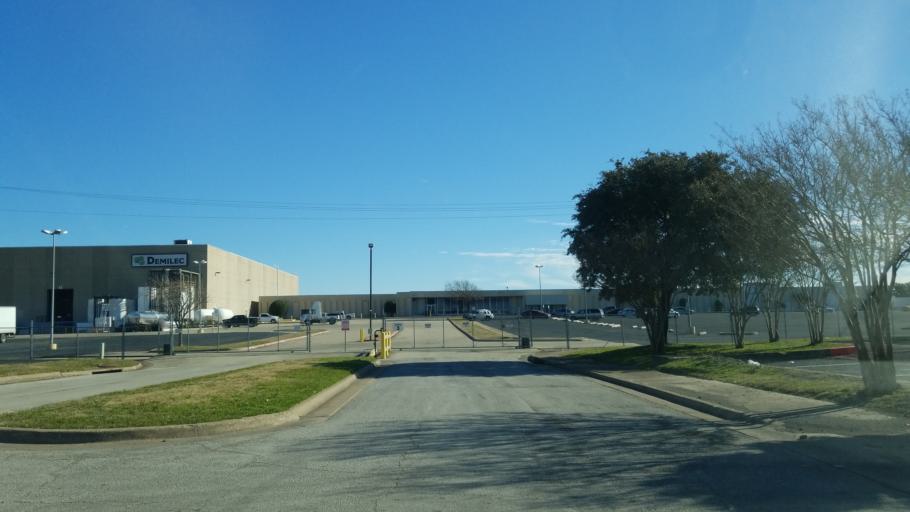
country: US
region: Texas
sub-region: Dallas County
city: Grand Prairie
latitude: 32.7428
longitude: -97.0513
